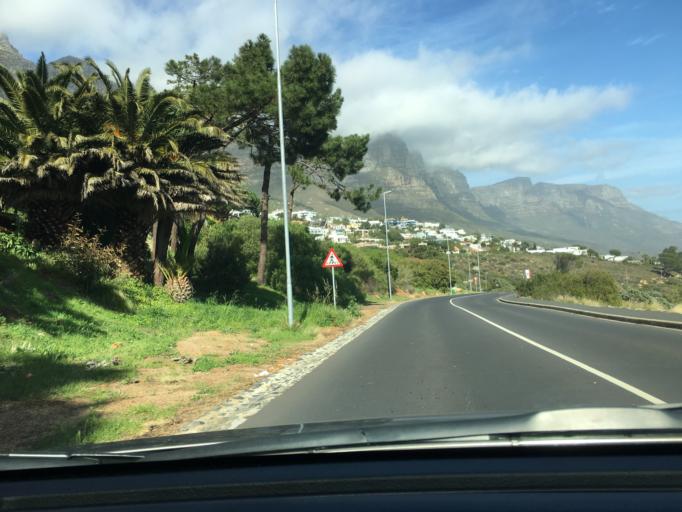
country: ZA
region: Western Cape
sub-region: City of Cape Town
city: Cape Town
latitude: -33.9554
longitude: 18.3856
